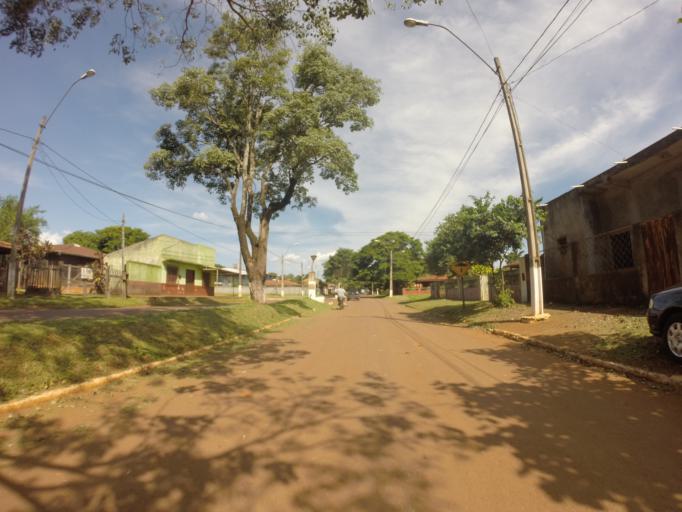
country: PY
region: Alto Parana
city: Ciudad del Este
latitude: -25.4032
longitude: -54.6477
